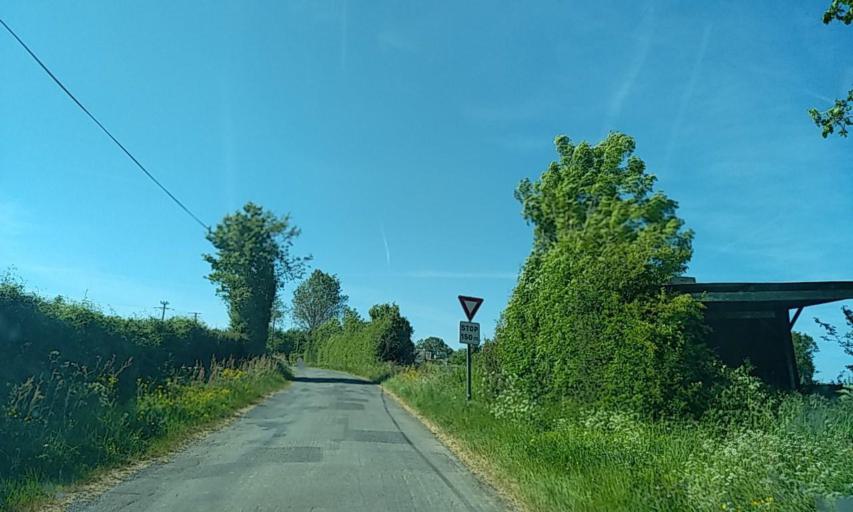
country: FR
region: Poitou-Charentes
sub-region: Departement des Deux-Sevres
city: Boisme
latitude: 46.7761
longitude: -0.4148
